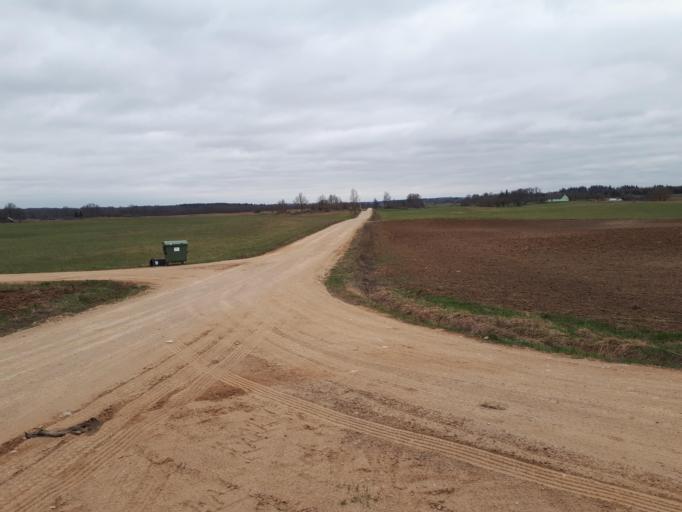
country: LT
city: Jieznas
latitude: 54.5481
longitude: 24.2589
